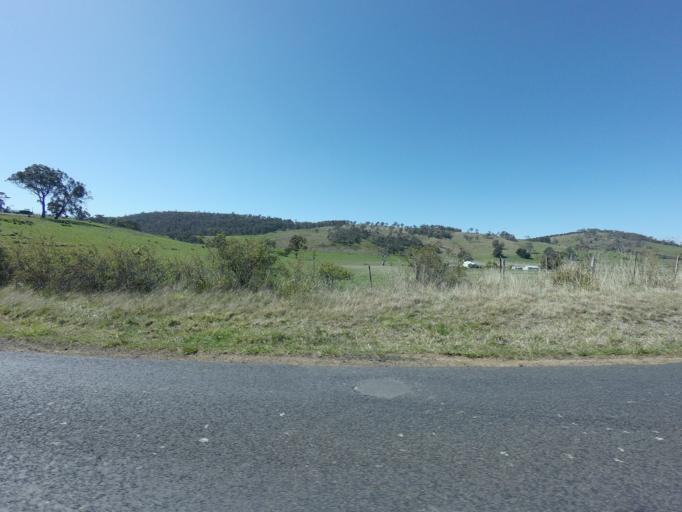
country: AU
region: Tasmania
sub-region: Derwent Valley
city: New Norfolk
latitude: -42.6321
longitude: 146.7353
